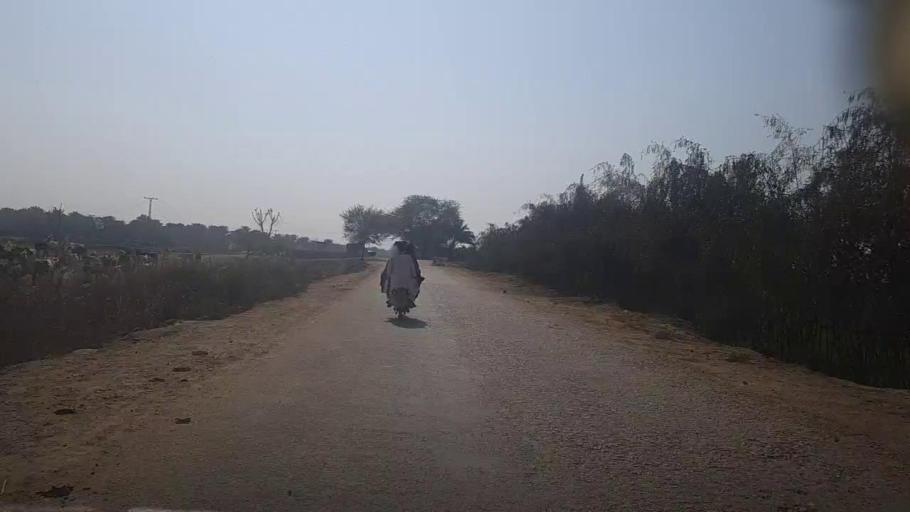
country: PK
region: Sindh
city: Khairpur
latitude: 27.4606
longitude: 68.8160
